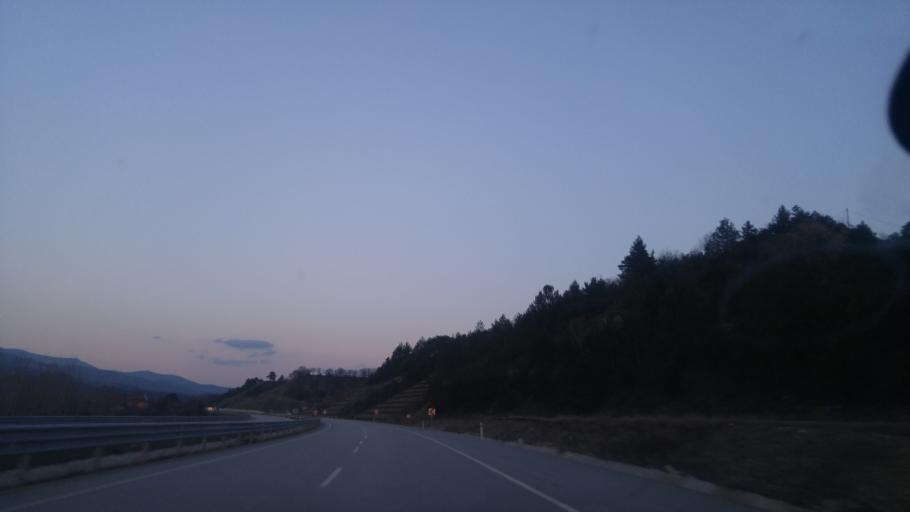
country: TR
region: Kastamonu
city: Igdir
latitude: 41.2312
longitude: 33.0398
